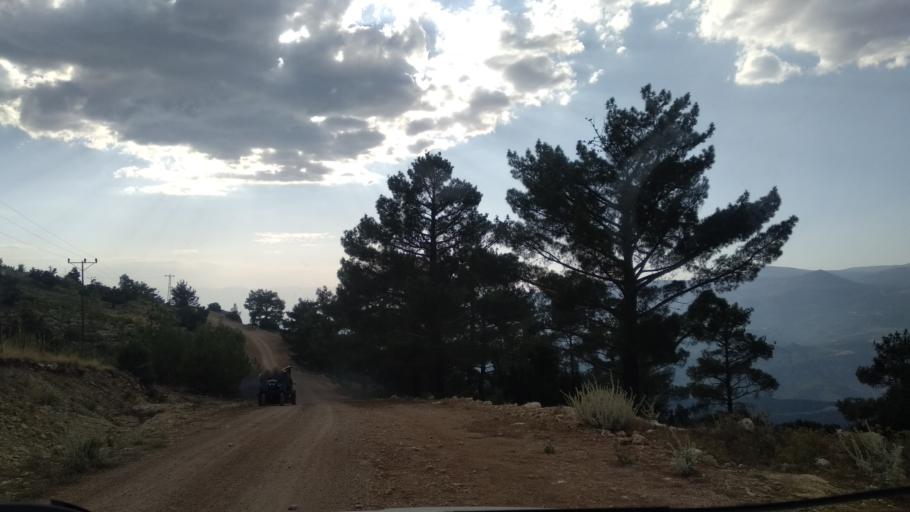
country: TR
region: Mersin
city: Sarikavak
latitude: 36.5979
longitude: 33.6922
